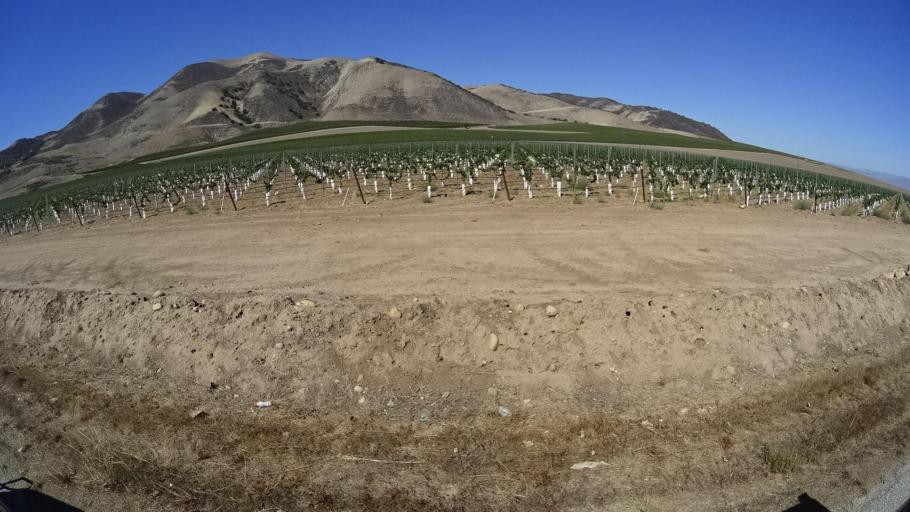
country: US
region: California
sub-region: Monterey County
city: Greenfield
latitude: 36.2926
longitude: -121.3121
